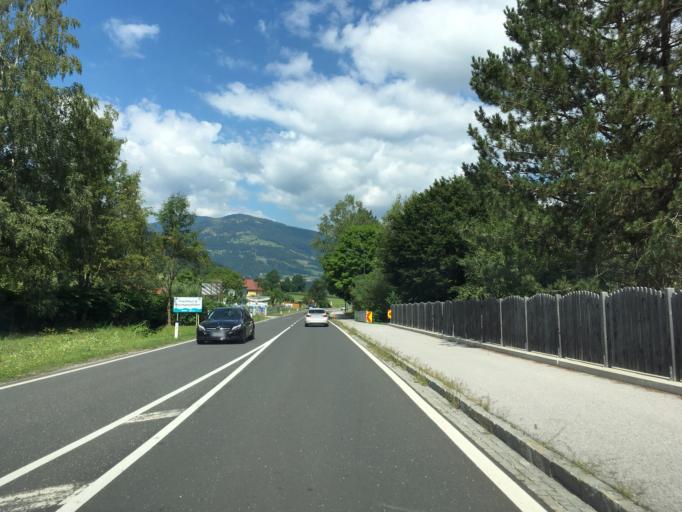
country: AT
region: Carinthia
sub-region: Politischer Bezirk Villach Land
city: Feld am See
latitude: 46.7802
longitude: 13.7415
